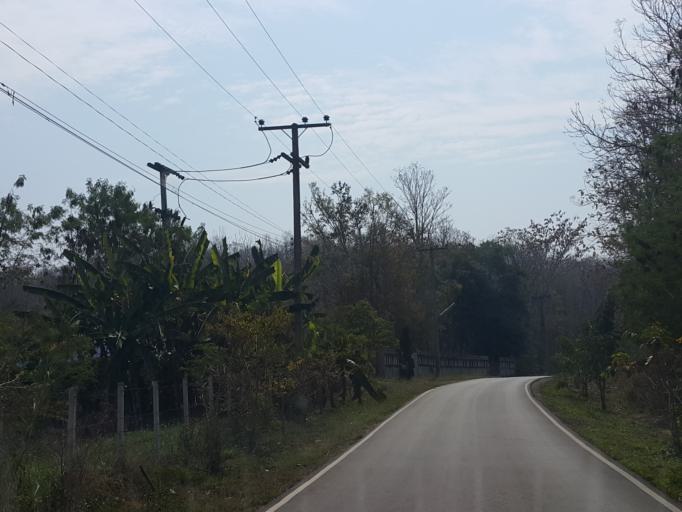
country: TH
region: Chiang Mai
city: Mae On
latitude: 18.8177
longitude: 99.2483
